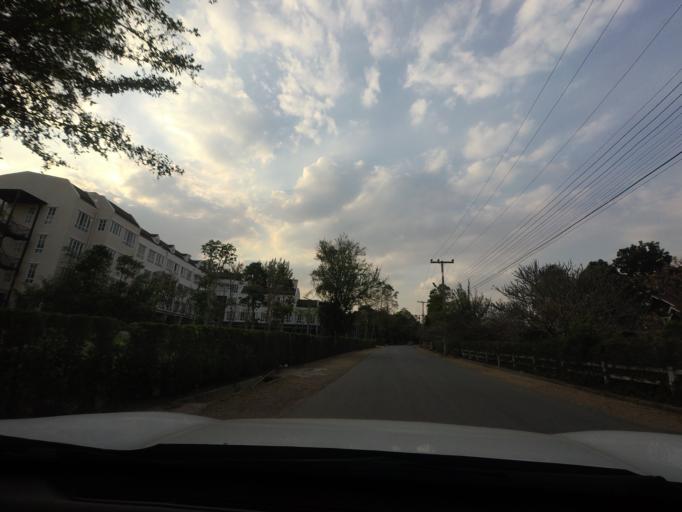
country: TH
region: Nakhon Ratchasima
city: Pak Chong
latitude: 14.5845
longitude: 101.4466
